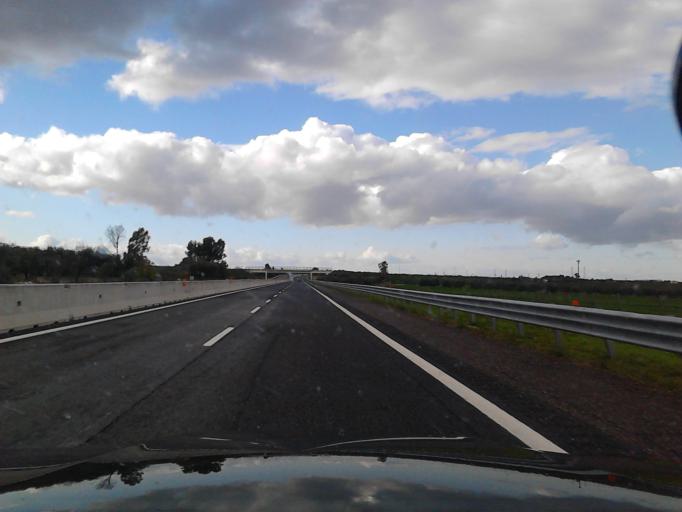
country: IT
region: Apulia
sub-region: Provincia di Barletta - Andria - Trani
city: Andria
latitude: 41.2516
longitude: 16.3093
